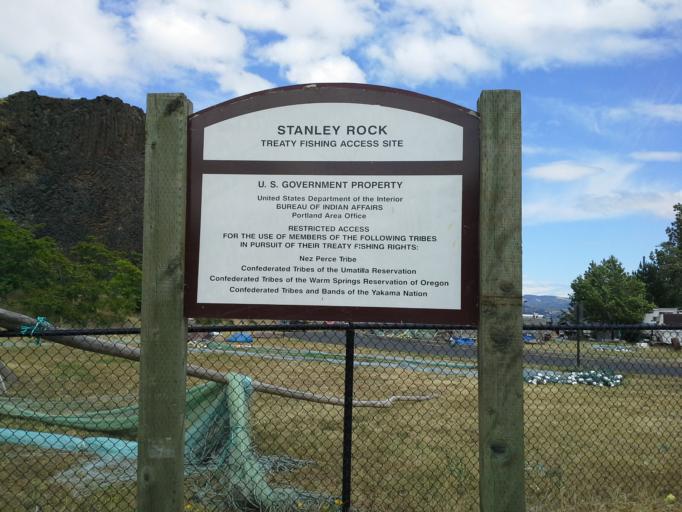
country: US
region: Washington
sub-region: Klickitat County
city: White Salmon
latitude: 45.7038
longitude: -121.4757
